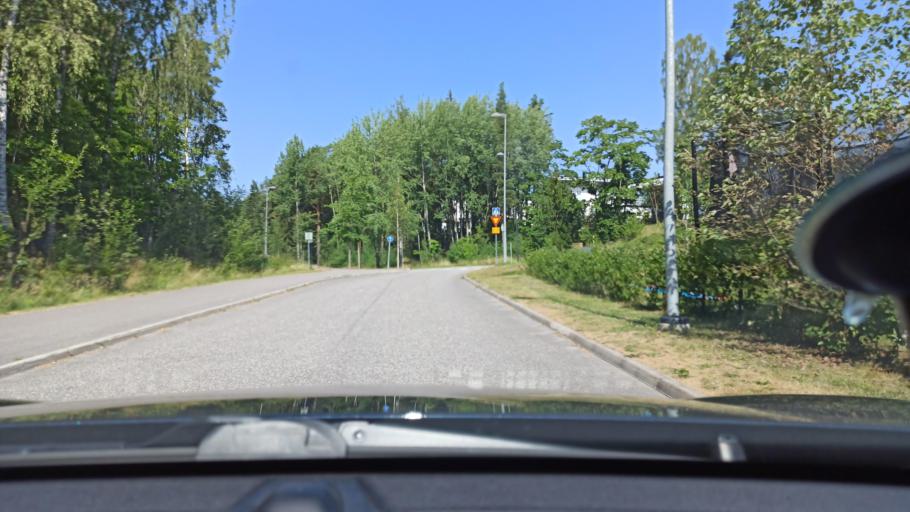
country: FI
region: Uusimaa
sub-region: Helsinki
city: Espoo
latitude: 60.1592
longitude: 24.5625
